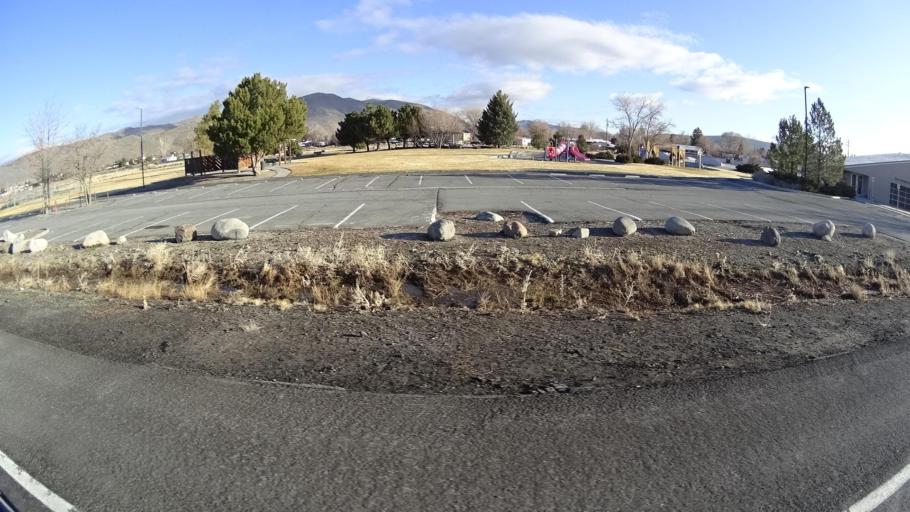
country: US
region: Nevada
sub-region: Washoe County
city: Cold Springs
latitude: 39.6756
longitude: -119.9766
